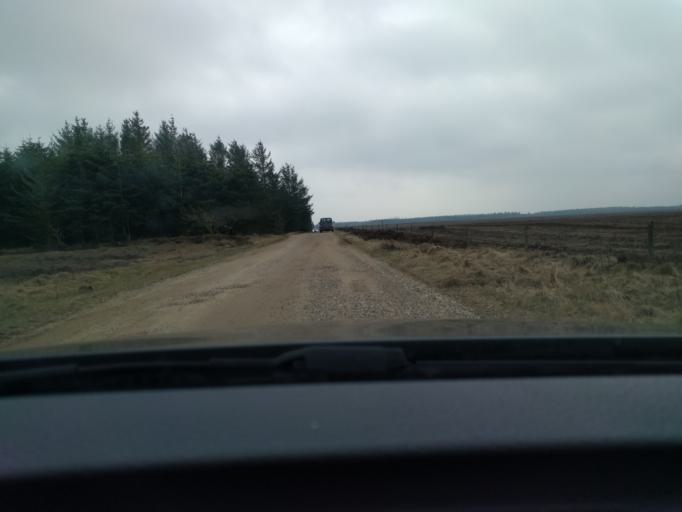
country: DK
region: Central Jutland
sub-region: Skive Kommune
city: Skive
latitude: 56.5081
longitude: 8.9450
